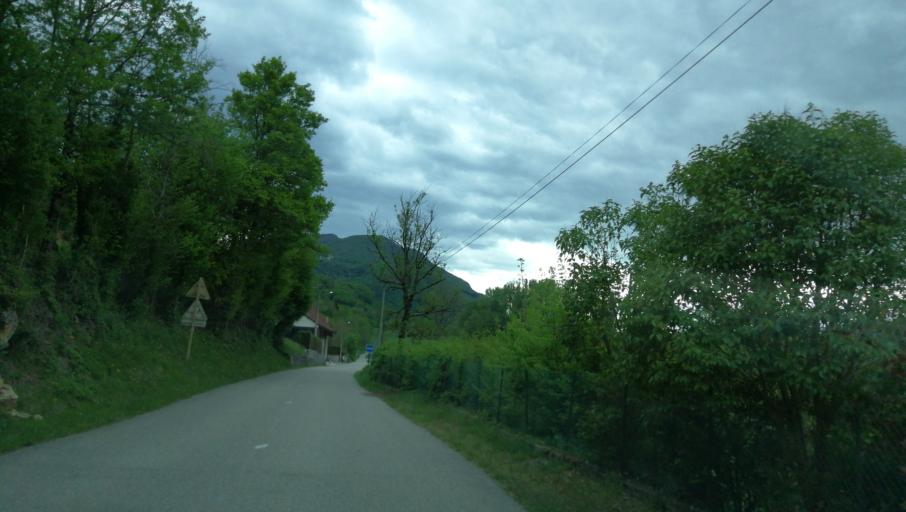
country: FR
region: Rhone-Alpes
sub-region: Departement de la Savoie
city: Chatillon
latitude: 45.7849
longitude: 5.8178
